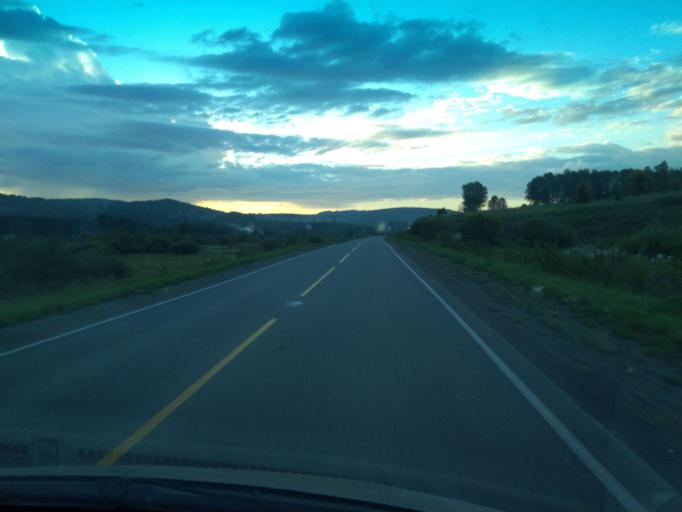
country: RU
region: Krasnoyarskiy
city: Zykovo
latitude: 55.8982
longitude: 93.1937
